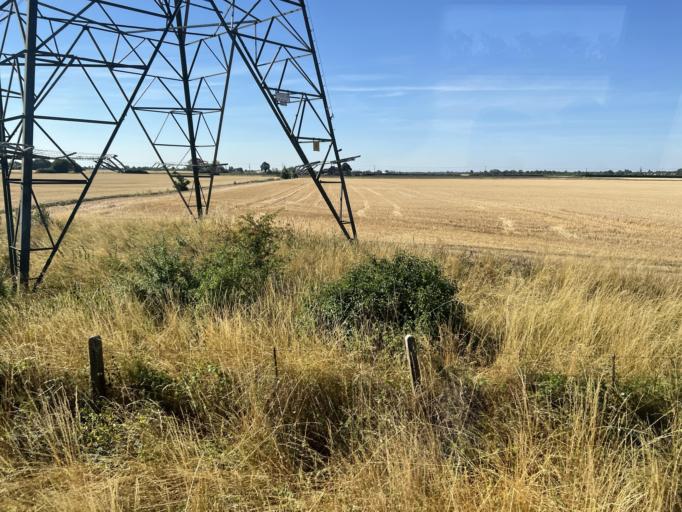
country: GB
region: England
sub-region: Lincolnshire
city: Heckington
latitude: 52.9730
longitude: -0.2708
